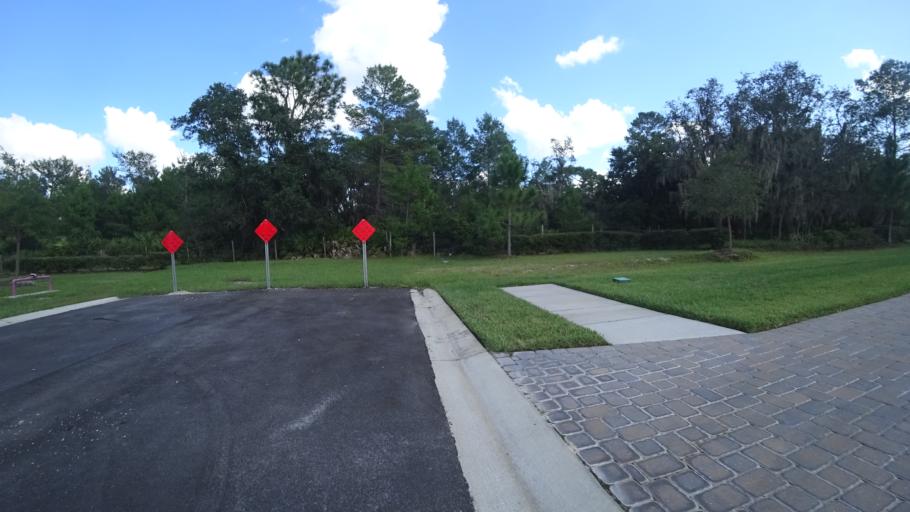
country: US
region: Florida
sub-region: Manatee County
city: Ellenton
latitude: 27.4920
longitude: -82.3684
